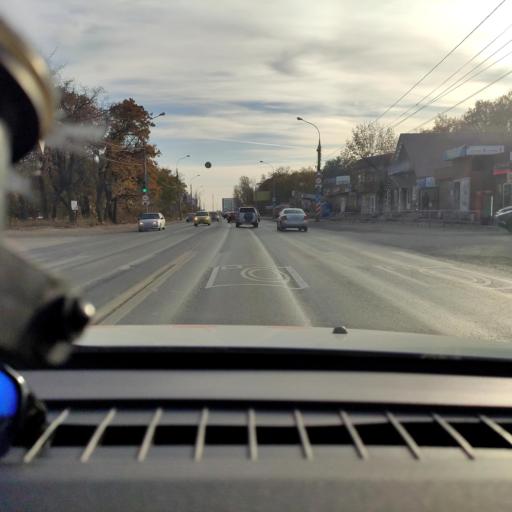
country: RU
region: Samara
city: Samara
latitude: 53.1314
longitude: 50.1726
